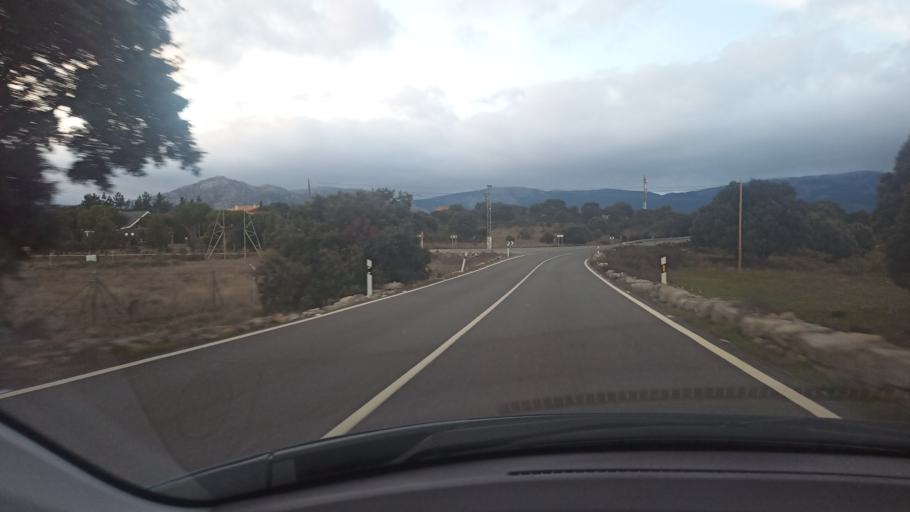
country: ES
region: Madrid
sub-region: Provincia de Madrid
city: Valdemorillo
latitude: 40.5374
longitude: -4.1008
